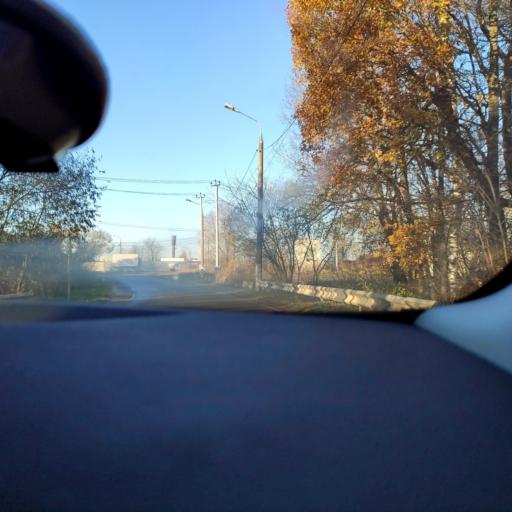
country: RU
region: Moskovskaya
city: Klimovsk
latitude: 55.3455
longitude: 37.5498
